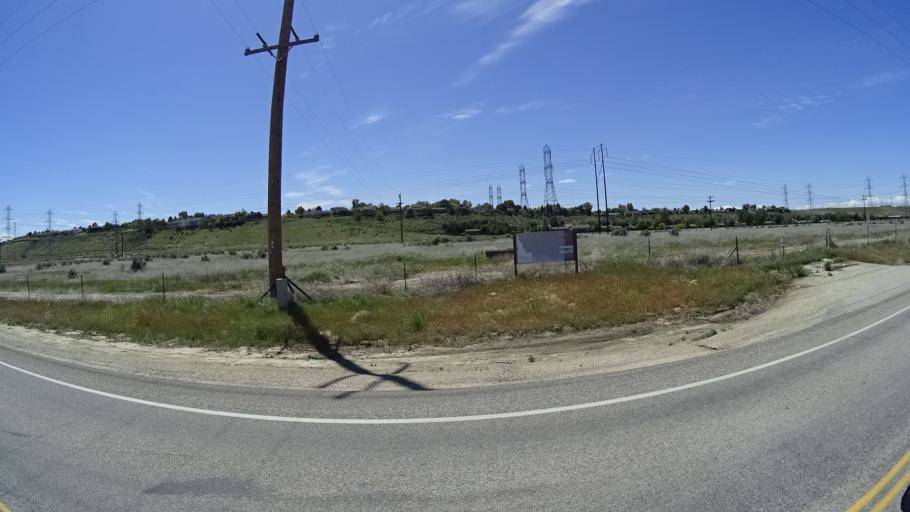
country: US
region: Idaho
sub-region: Ada County
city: Boise
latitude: 43.5606
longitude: -116.1443
